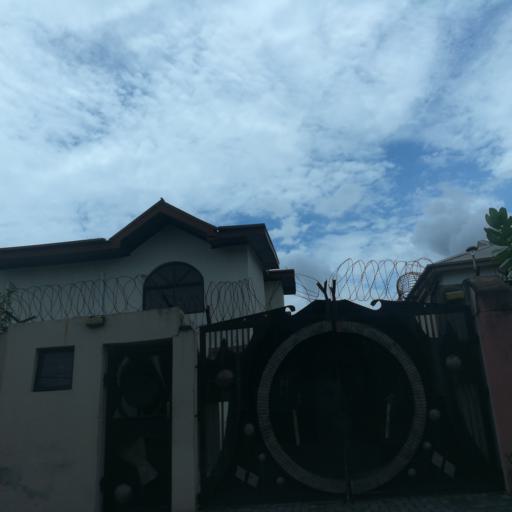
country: NG
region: Lagos
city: Ikoyi
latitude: 6.4440
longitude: 3.4681
